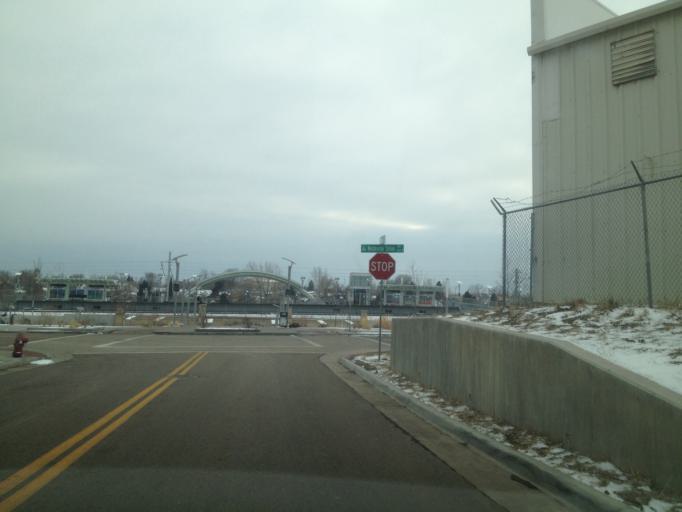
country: US
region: Colorado
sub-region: Adams County
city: Westminster
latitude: 39.8236
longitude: -105.0285
